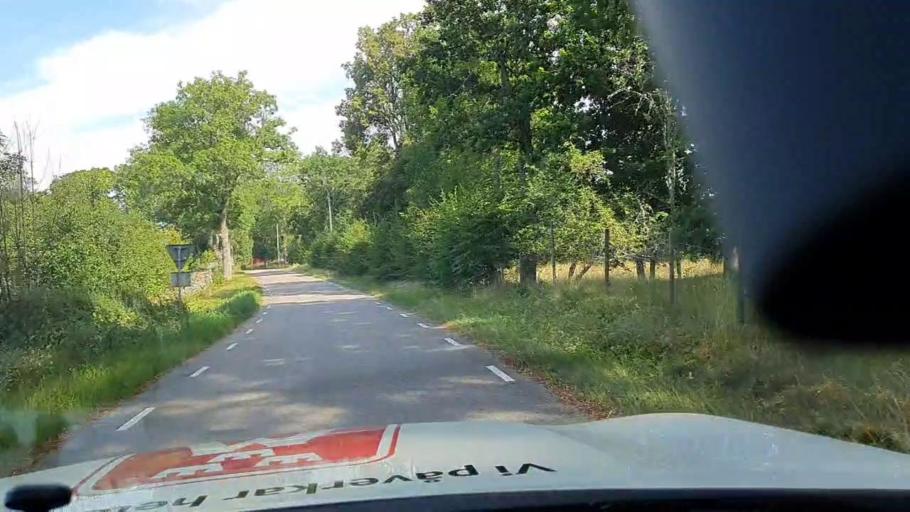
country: SE
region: Soedermanland
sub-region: Strangnas Kommun
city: Akers Styckebruk
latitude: 59.2707
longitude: 16.9819
